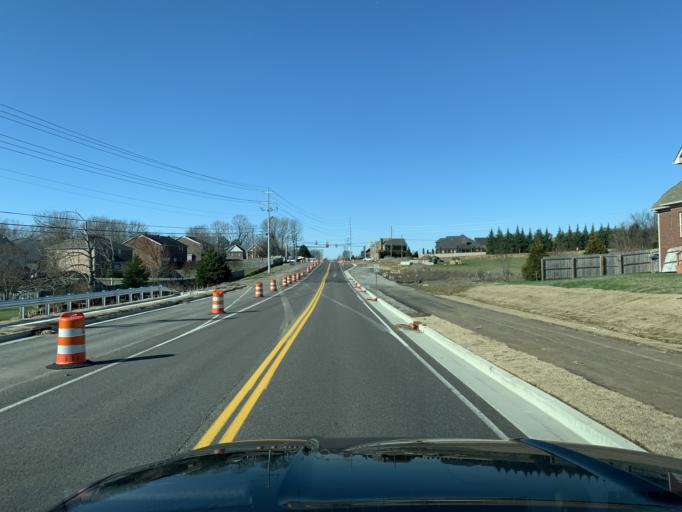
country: US
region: Tennessee
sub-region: Maury County
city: Spring Hill
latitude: 35.7528
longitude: -86.8816
